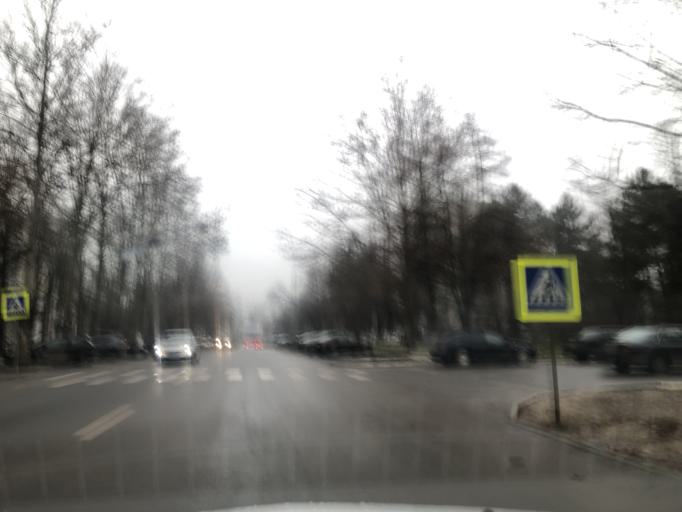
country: MD
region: Chisinau
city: Chisinau
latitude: 47.0504
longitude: 28.8589
